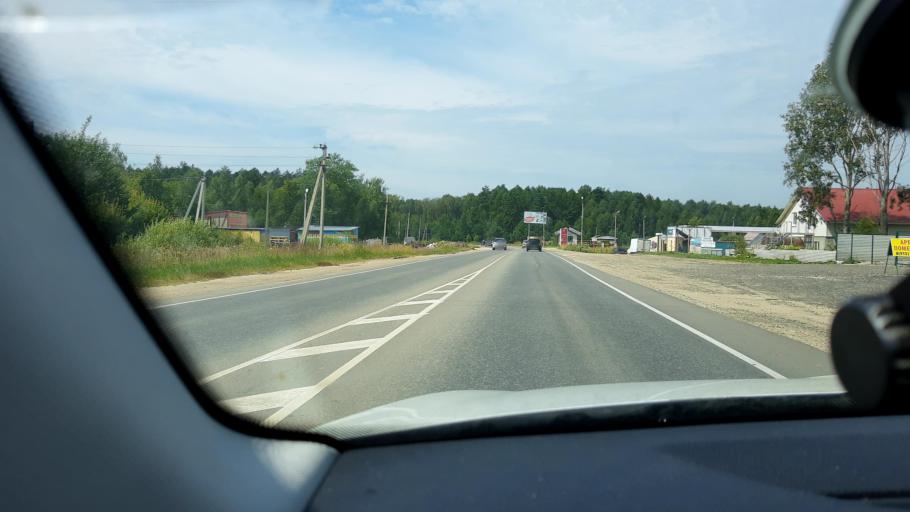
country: RU
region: Tula
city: Zaokskiy
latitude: 54.7470
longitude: 37.4066
